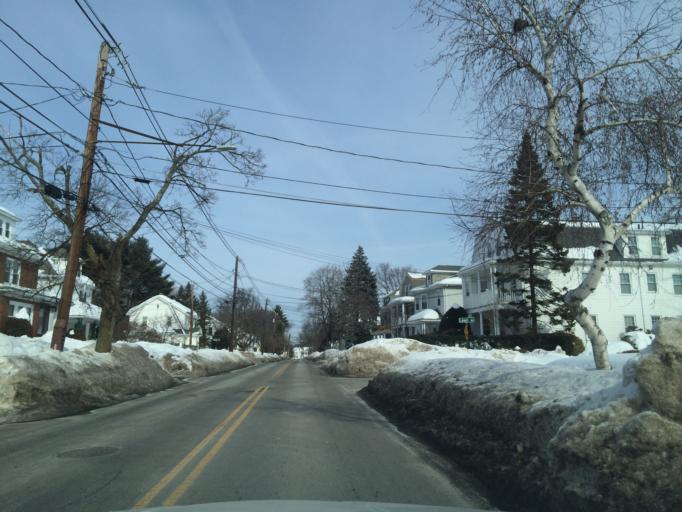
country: US
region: Massachusetts
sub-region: Middlesex County
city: Newton
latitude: 42.3618
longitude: -71.2091
